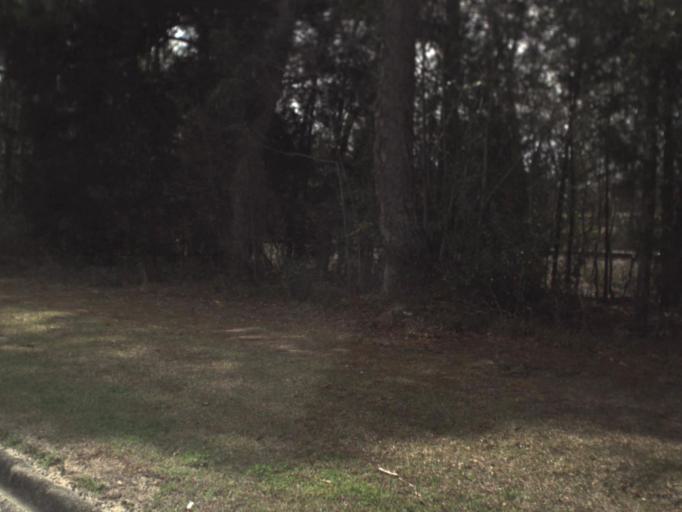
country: US
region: Florida
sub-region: Washington County
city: Chipley
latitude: 30.7010
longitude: -85.3919
